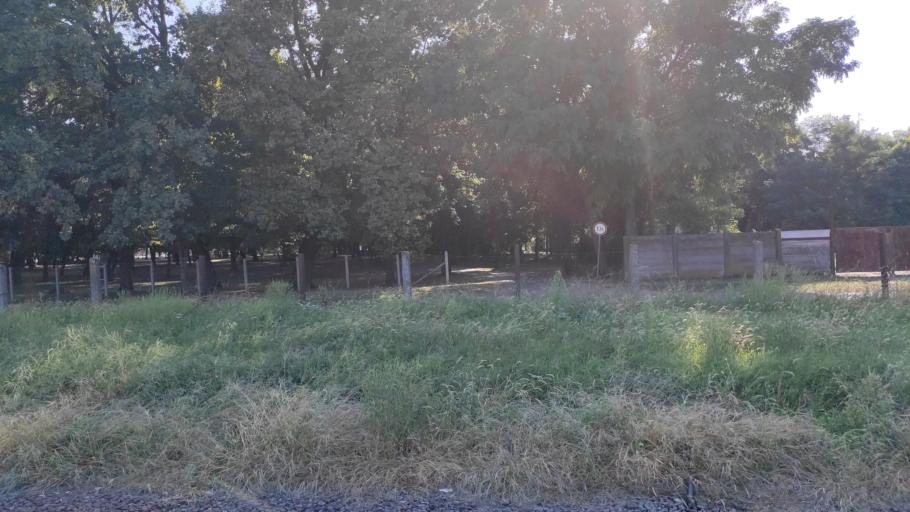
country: HU
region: Bekes
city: Lokoshaza
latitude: 46.4308
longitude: 21.2388
